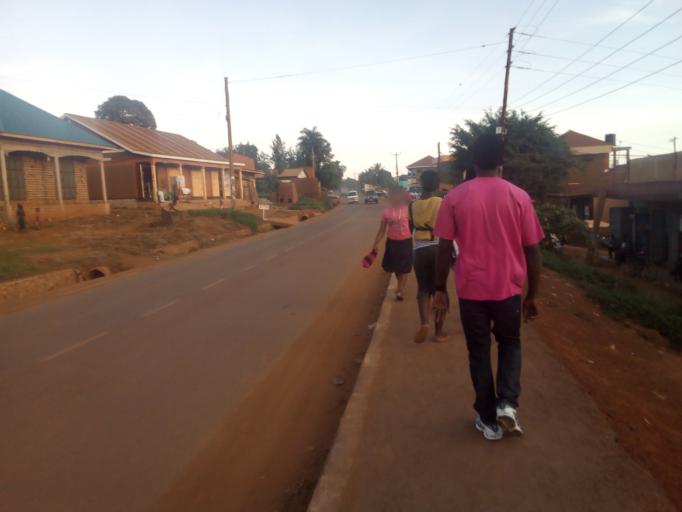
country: UG
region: Central Region
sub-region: Wakiso District
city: Kajansi
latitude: 0.2430
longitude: 32.5724
